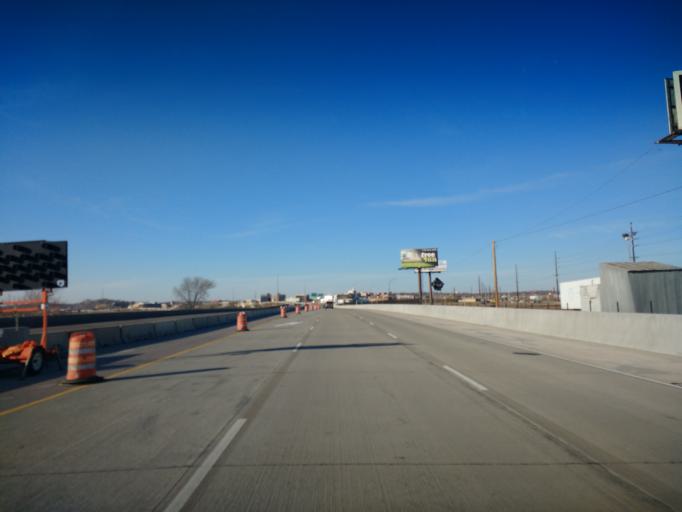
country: US
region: Iowa
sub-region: Woodbury County
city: Sioux City
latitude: 42.4792
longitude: -96.3869
